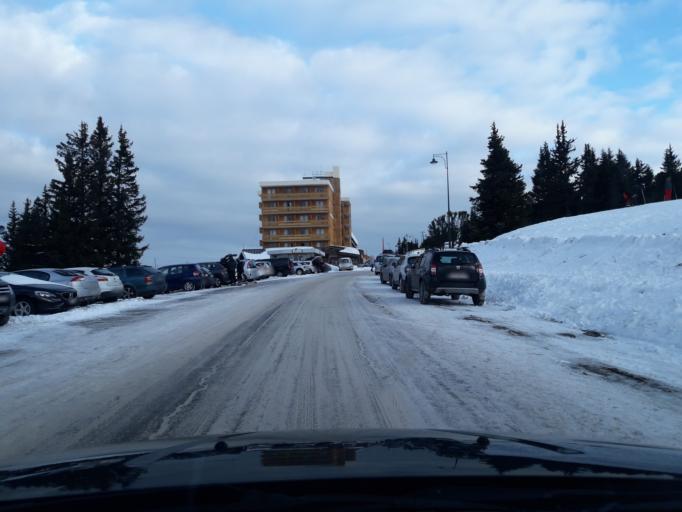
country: FR
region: Rhone-Alpes
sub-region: Departement de l'Isere
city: Vaulnaveys-le-Bas
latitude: 45.1126
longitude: 5.8785
